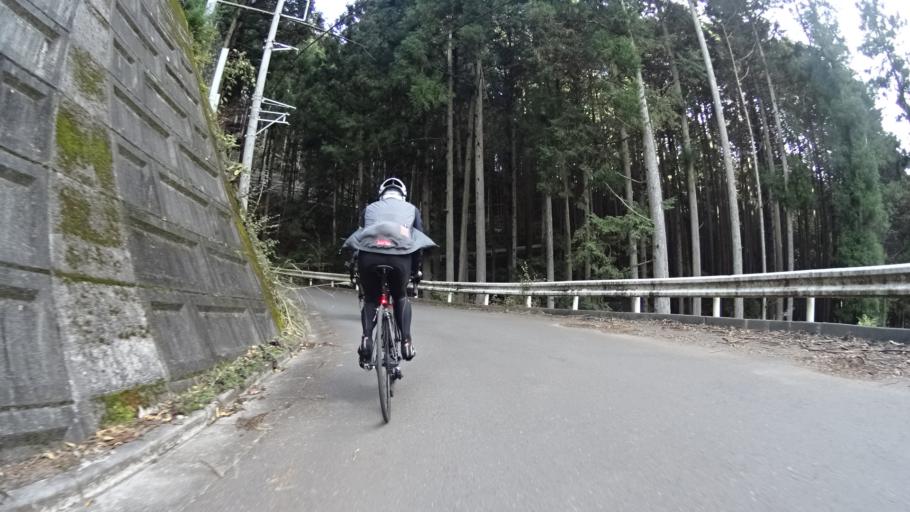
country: JP
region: Saitama
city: Chichibu
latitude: 35.9143
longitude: 139.1774
